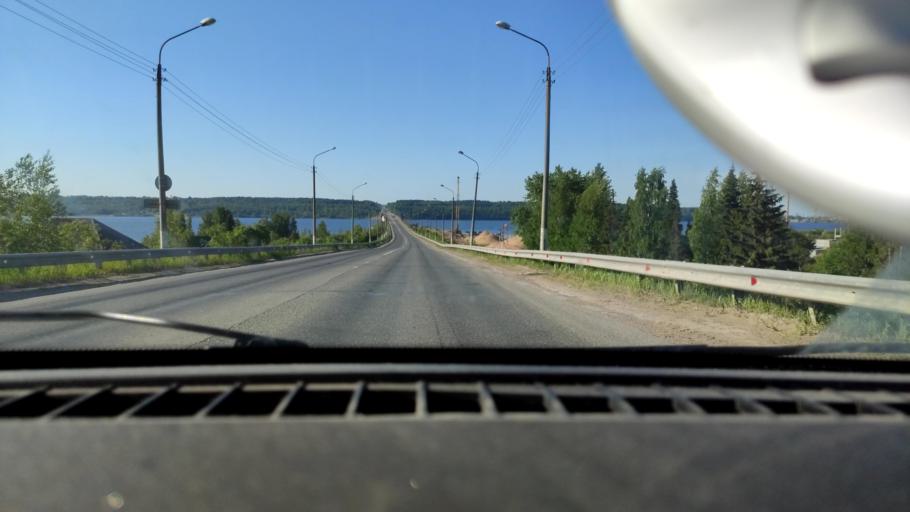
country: RU
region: Perm
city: Polazna
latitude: 58.1778
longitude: 56.4137
